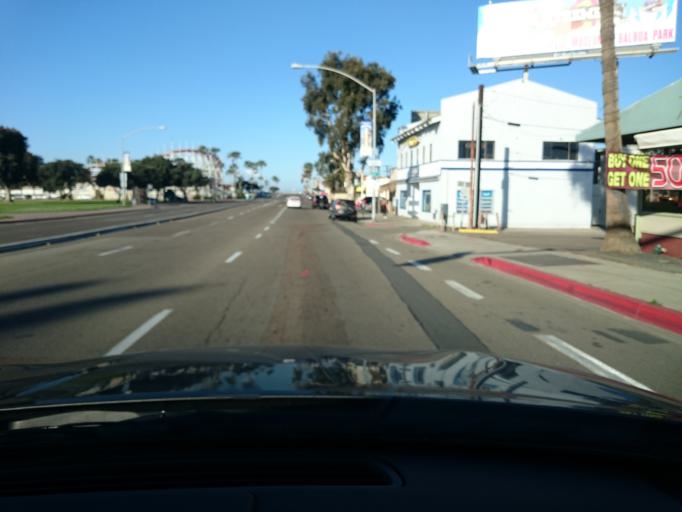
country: US
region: California
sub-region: San Diego County
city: La Jolla
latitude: 32.7721
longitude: -117.2497
